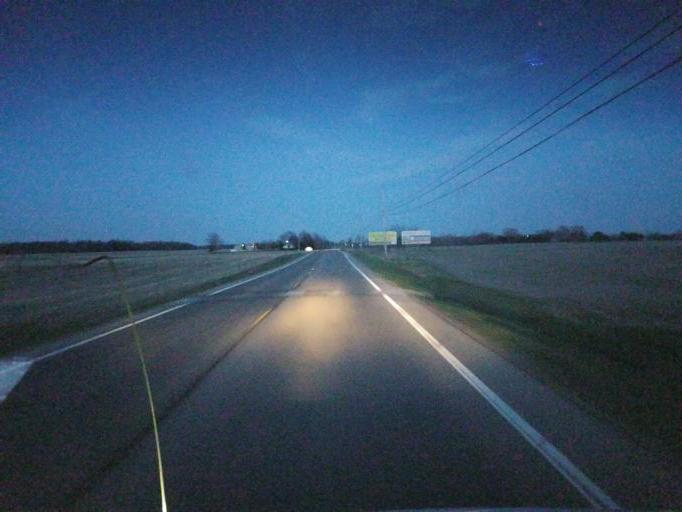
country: US
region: Ohio
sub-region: Logan County
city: Bellefontaine
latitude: 40.3650
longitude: -83.8226
